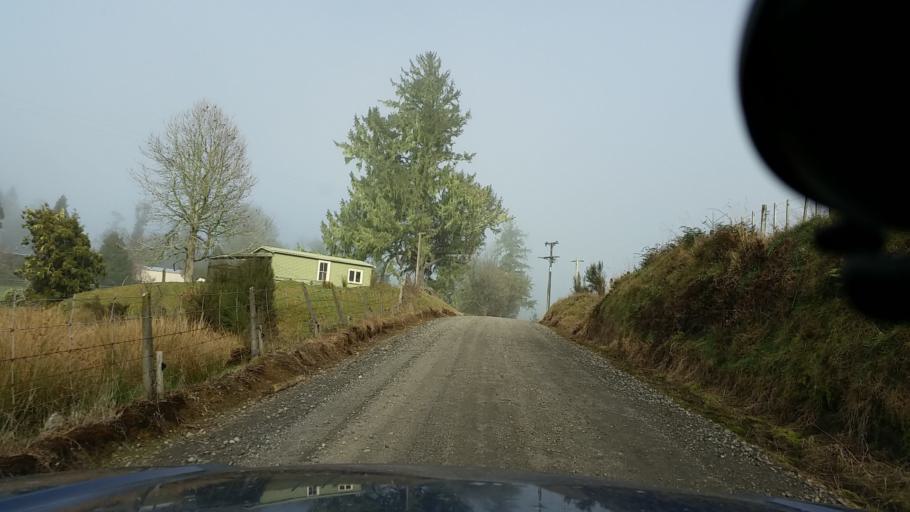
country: NZ
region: Taranaki
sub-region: New Plymouth District
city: Waitara
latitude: -38.9931
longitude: 174.7758
